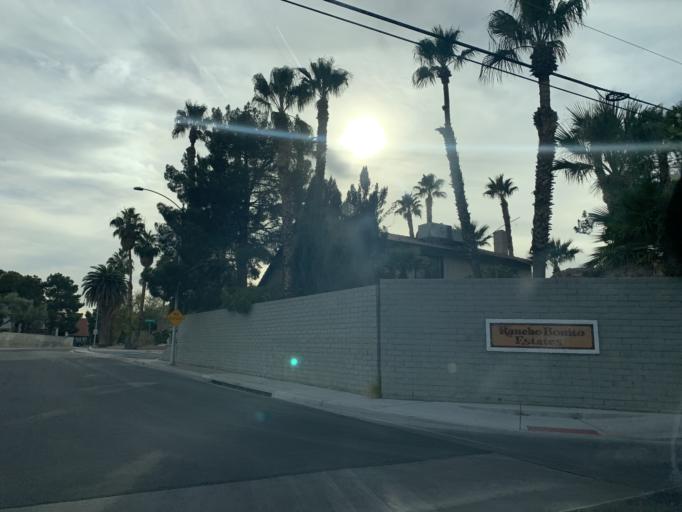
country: US
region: Nevada
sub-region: Clark County
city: Las Vegas
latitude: 36.1516
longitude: -115.1752
